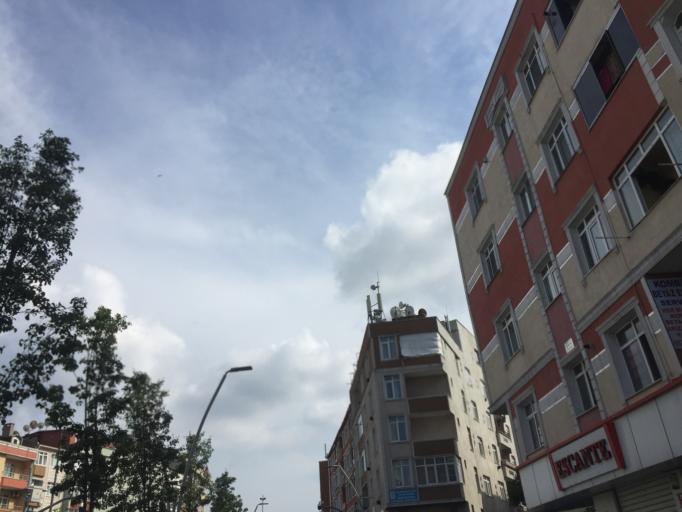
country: TR
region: Istanbul
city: Zeytinburnu
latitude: 40.9992
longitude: 28.9045
